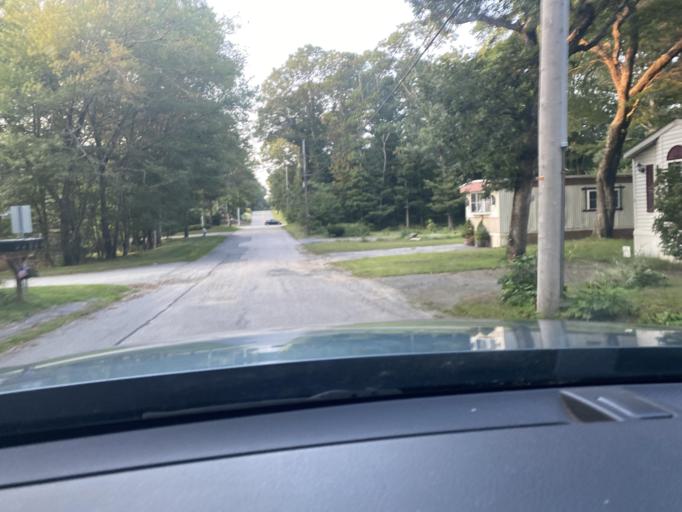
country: US
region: Massachusetts
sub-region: Barnstable County
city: Mashpee
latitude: 41.6151
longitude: -70.5145
